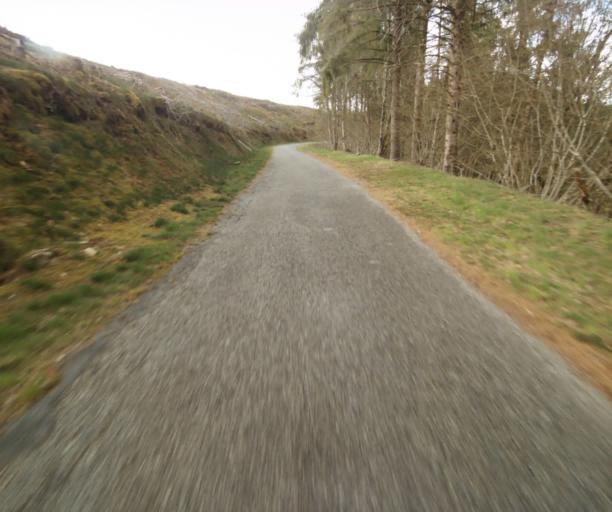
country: FR
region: Limousin
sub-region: Departement de la Correze
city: Egletons
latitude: 45.2745
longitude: 1.9945
